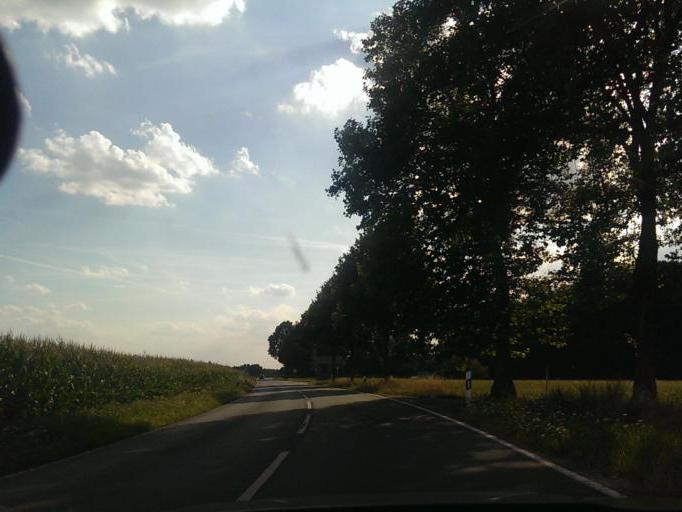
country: DE
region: North Rhine-Westphalia
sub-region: Regierungsbezirk Detmold
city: Delbruck
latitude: 51.7254
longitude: 8.5387
